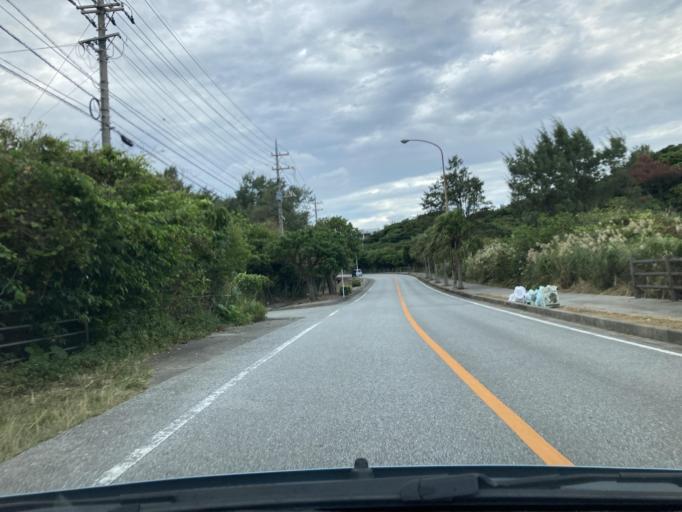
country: JP
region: Okinawa
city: Ishikawa
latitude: 26.4362
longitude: 127.7811
